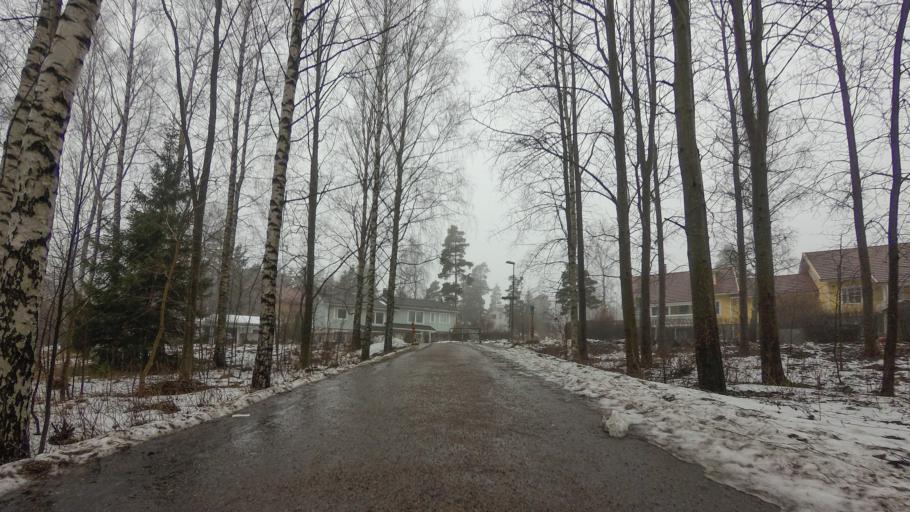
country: FI
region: Uusimaa
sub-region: Helsinki
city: Vantaa
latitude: 60.2137
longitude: 25.0479
